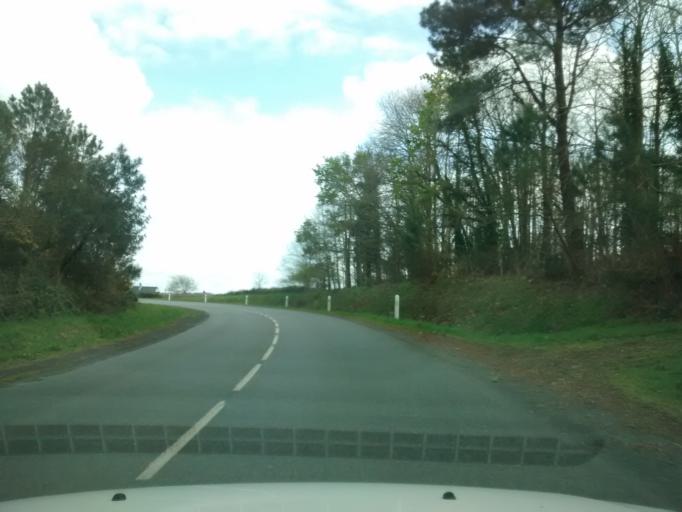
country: FR
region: Brittany
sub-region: Departement du Morbihan
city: Guidel-Plage
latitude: 47.7931
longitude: -3.5241
